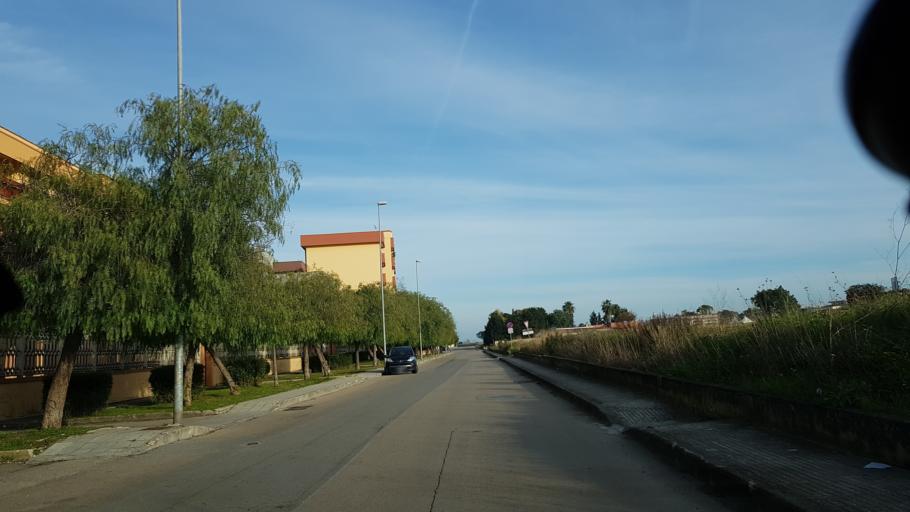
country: IT
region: Apulia
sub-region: Provincia di Brindisi
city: Brindisi
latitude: 40.6164
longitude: 17.9231
